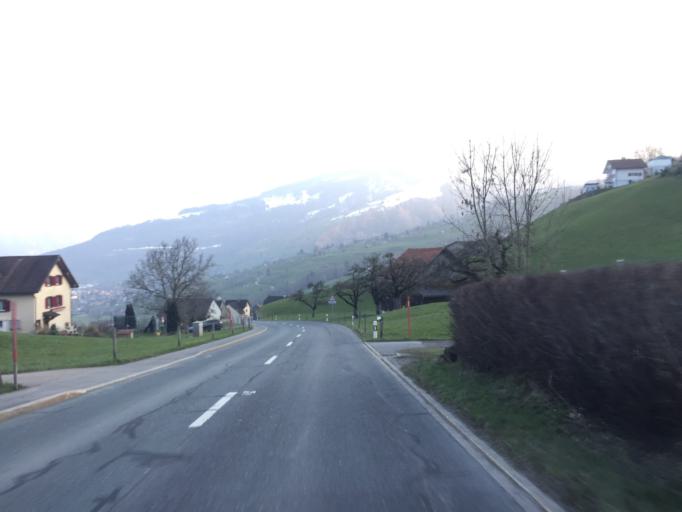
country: CH
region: Saint Gallen
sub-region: Wahlkreis Werdenberg
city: Gams
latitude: 47.2005
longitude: 9.4318
